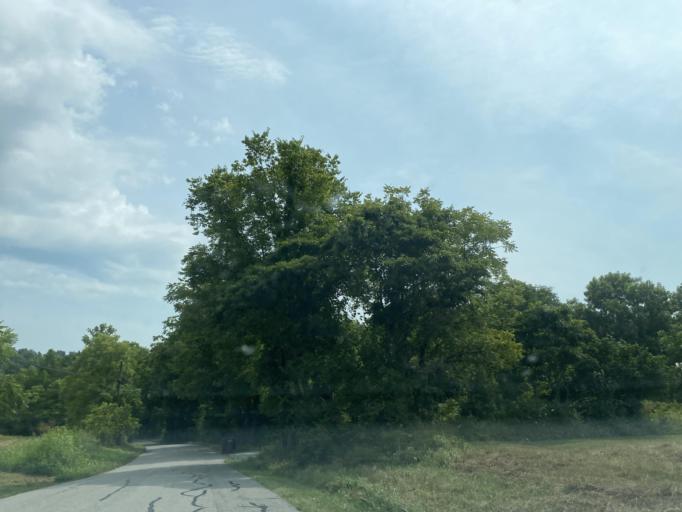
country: US
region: Kentucky
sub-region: Pendleton County
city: Falmouth
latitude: 38.7961
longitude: -84.3357
